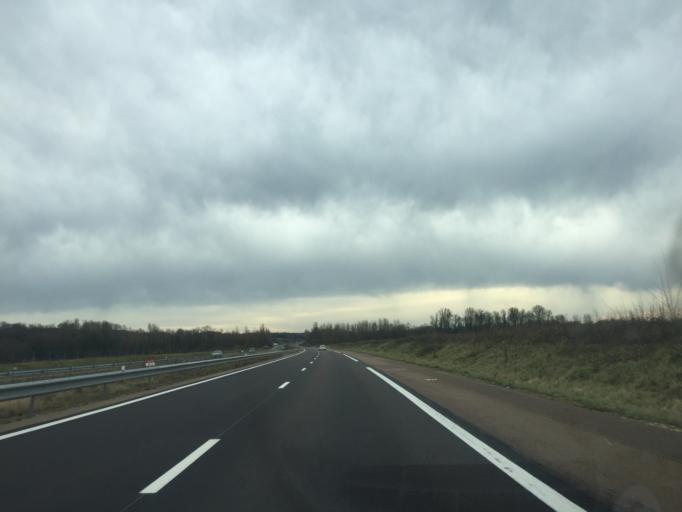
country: FR
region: Franche-Comte
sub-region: Departement du Jura
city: Bletterans
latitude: 46.7535
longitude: 5.5091
